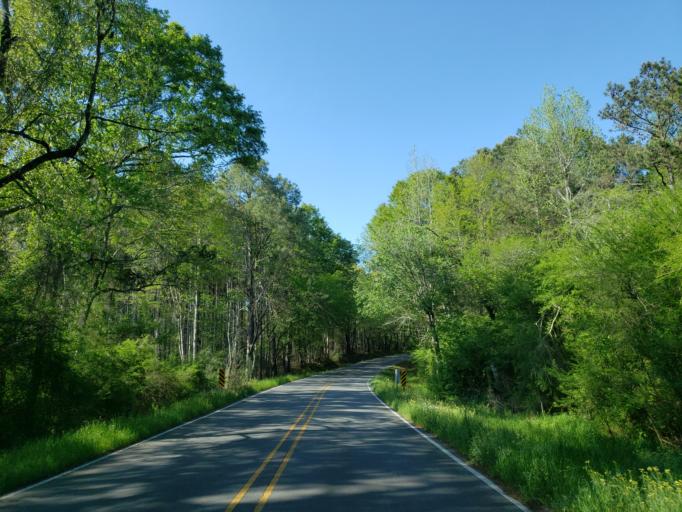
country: US
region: Mississippi
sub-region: Forrest County
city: Rawls Springs
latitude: 31.5072
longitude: -89.3603
